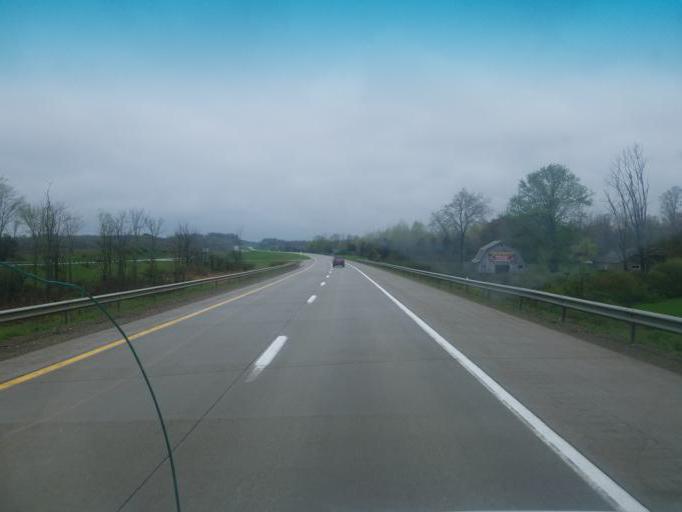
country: US
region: Pennsylvania
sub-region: Erie County
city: North East
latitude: 42.1300
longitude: -79.7674
